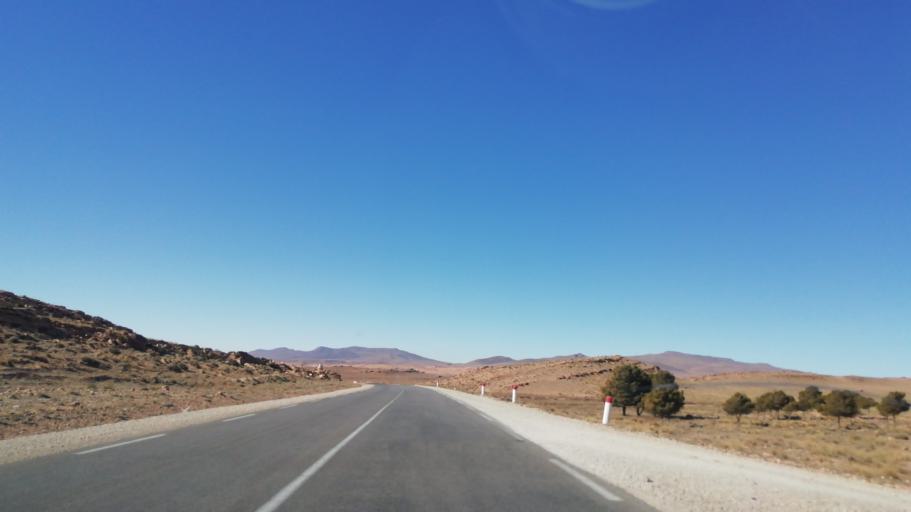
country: DZ
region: El Bayadh
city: El Bayadh
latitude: 33.6106
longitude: 1.2316
